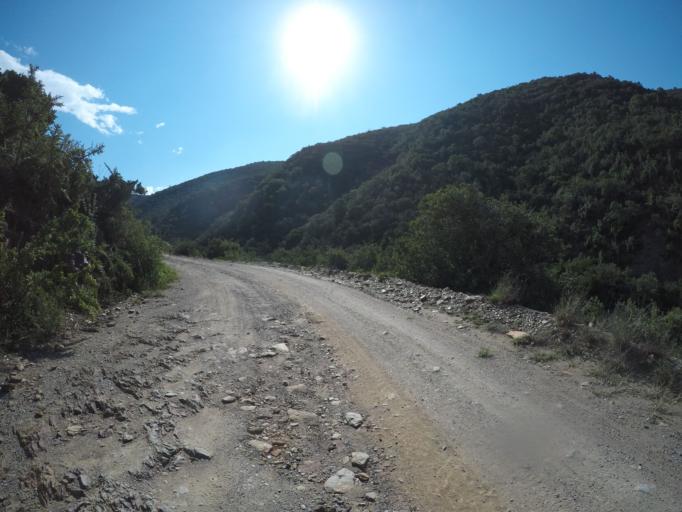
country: ZA
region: Eastern Cape
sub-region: Cacadu District Municipality
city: Kareedouw
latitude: -33.6541
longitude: 24.3558
